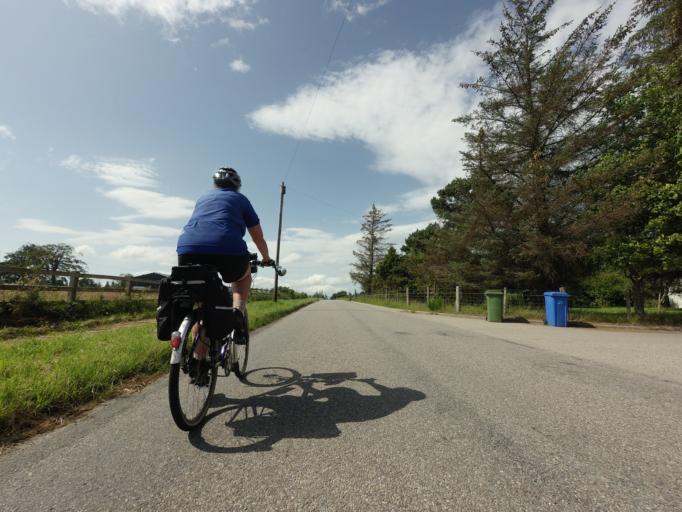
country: GB
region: Scotland
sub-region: Highland
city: Fortrose
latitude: 57.4874
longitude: -4.1003
